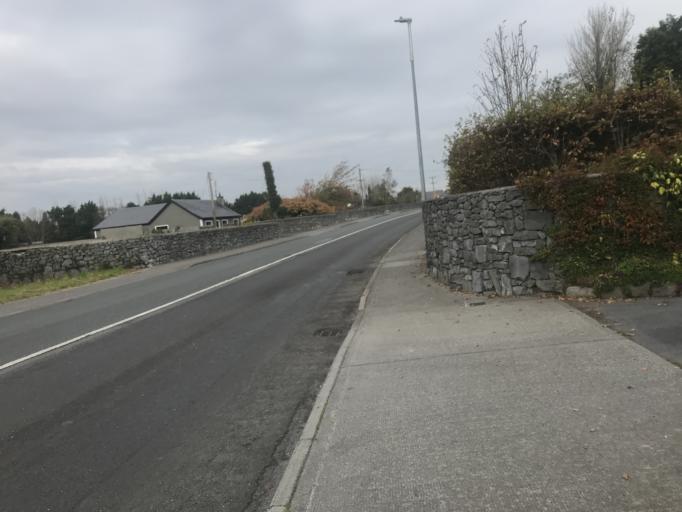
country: IE
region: Connaught
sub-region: County Galway
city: Gaillimh
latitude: 53.2955
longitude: -9.0536
